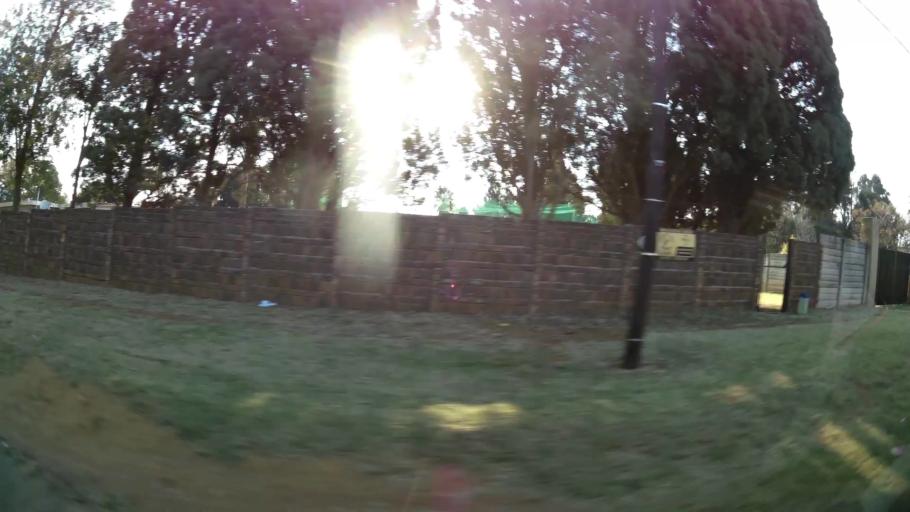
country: ZA
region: Gauteng
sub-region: Ekurhuleni Metropolitan Municipality
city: Benoni
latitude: -26.1439
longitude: 28.3614
